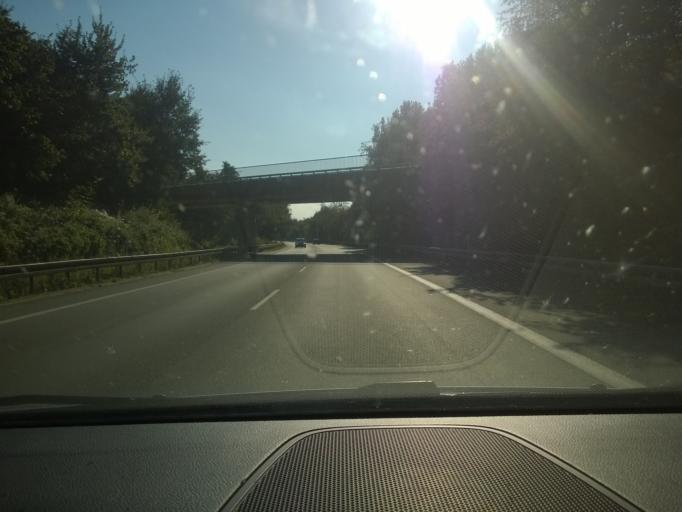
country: DE
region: North Rhine-Westphalia
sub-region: Regierungsbezirk Munster
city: Borken
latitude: 51.8624
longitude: 6.8407
